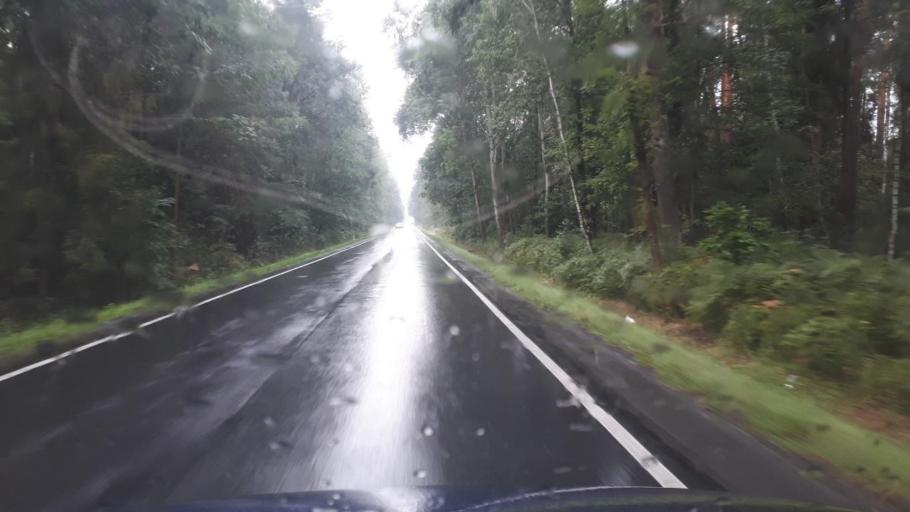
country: PL
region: Silesian Voivodeship
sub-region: Powiat tarnogorski
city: Tworog
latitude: 50.5292
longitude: 18.6662
